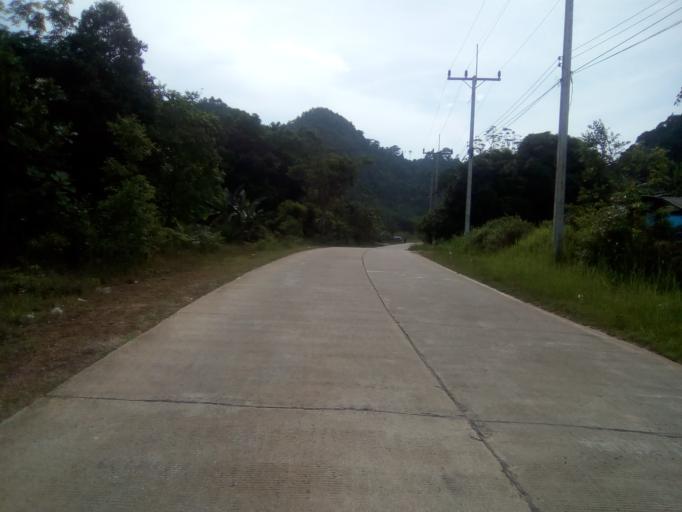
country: TH
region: Krabi
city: Saladan
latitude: 7.5818
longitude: 99.0639
